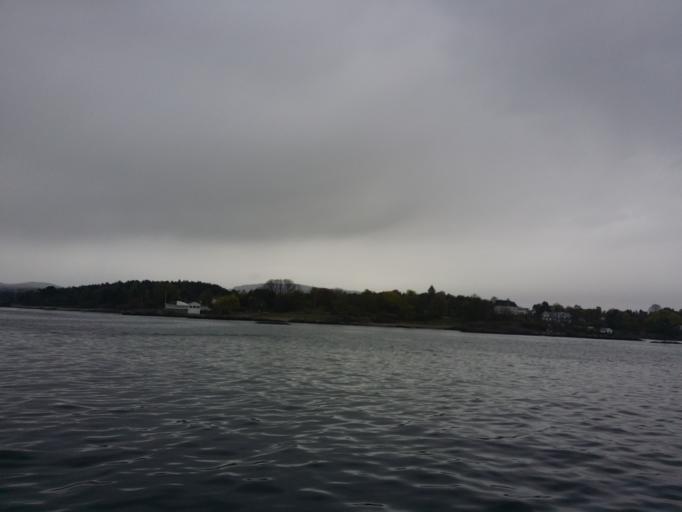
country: NO
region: Oslo
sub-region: Oslo
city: Sjolyststranda
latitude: 59.8917
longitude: 10.6759
